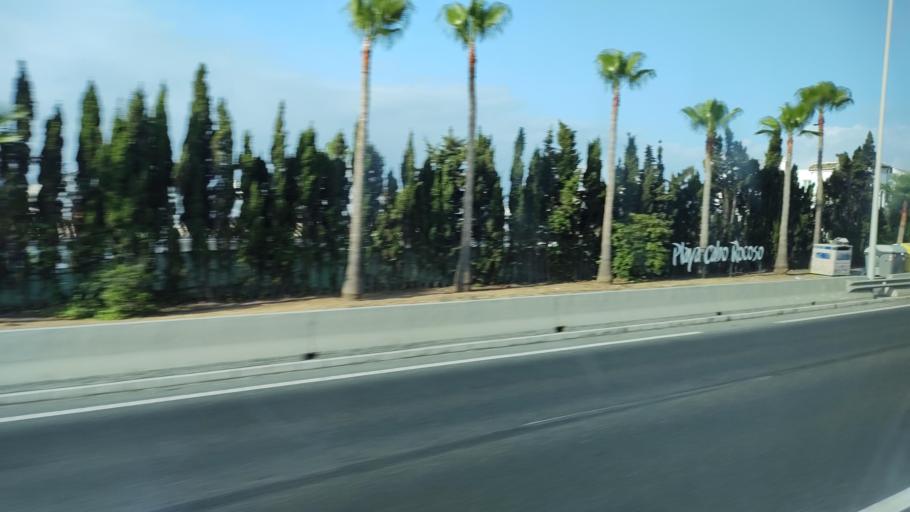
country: ES
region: Andalusia
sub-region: Provincia de Malaga
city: Fuengirola
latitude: 36.4912
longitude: -4.6975
